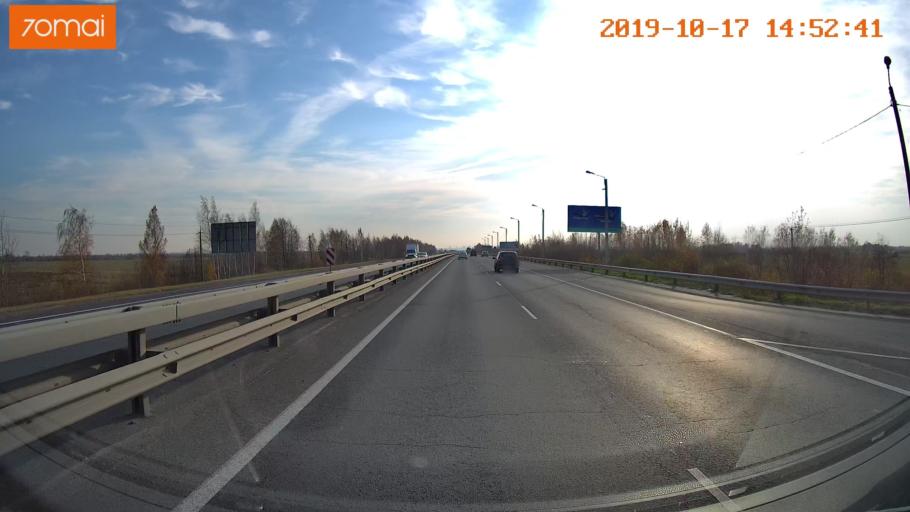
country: RU
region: Rjazan
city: Polyany
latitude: 54.7042
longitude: 39.8439
